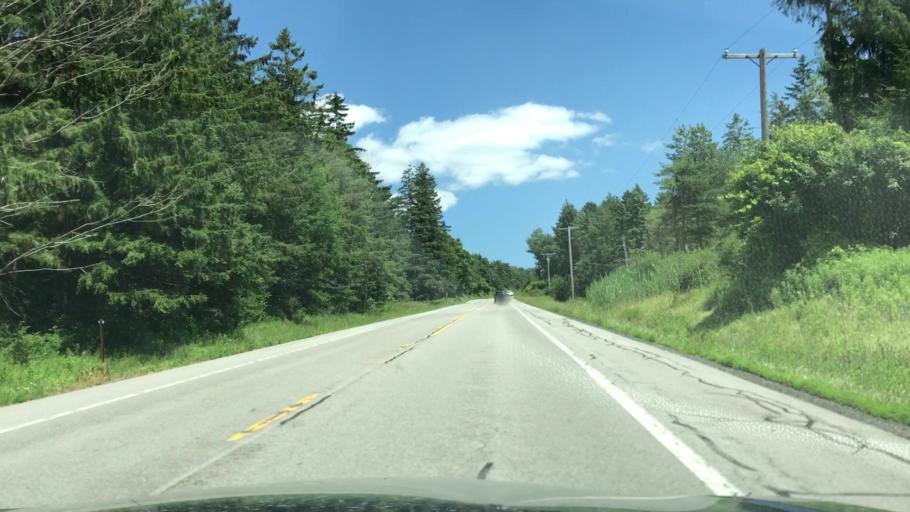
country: US
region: New York
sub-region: Wyoming County
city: Warsaw
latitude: 42.7490
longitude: -78.2415
